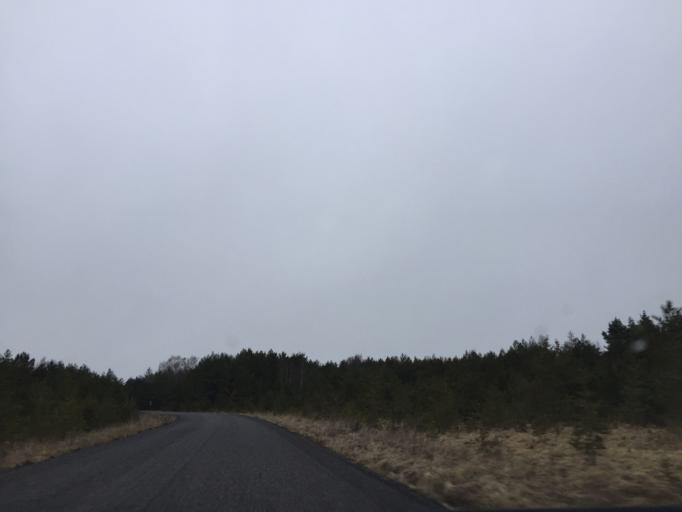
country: EE
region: Laeaene
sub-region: Ridala Parish
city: Uuemoisa
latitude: 58.6721
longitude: 23.5613
